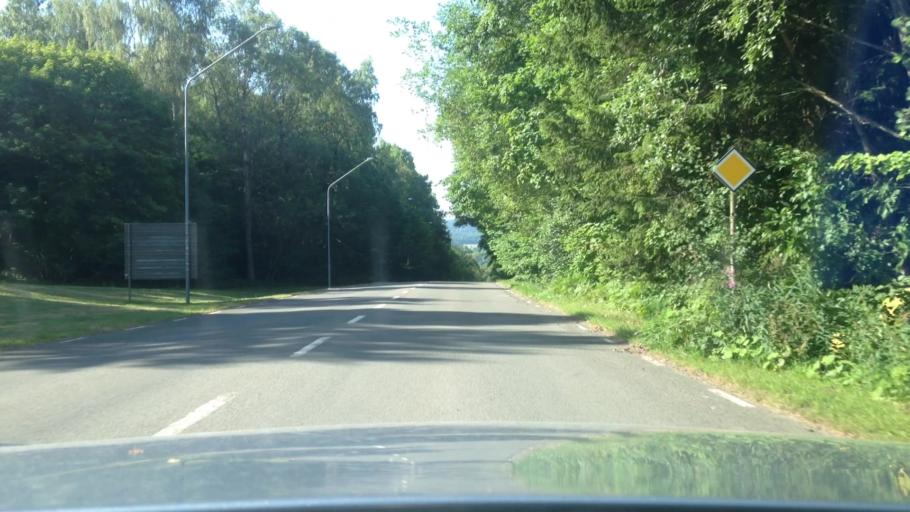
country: SE
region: Vaestra Goetaland
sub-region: Skovde Kommun
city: Skoevde
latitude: 58.4010
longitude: 13.8191
